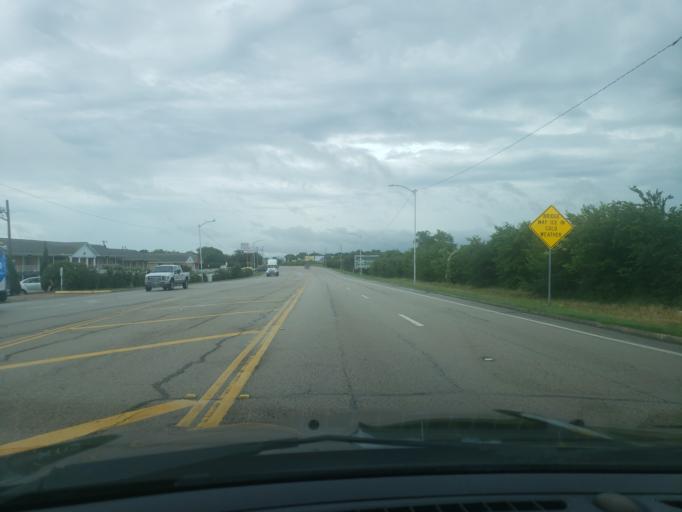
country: US
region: Texas
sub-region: Dallas County
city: Grand Prairie
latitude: 32.7419
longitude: -97.0183
